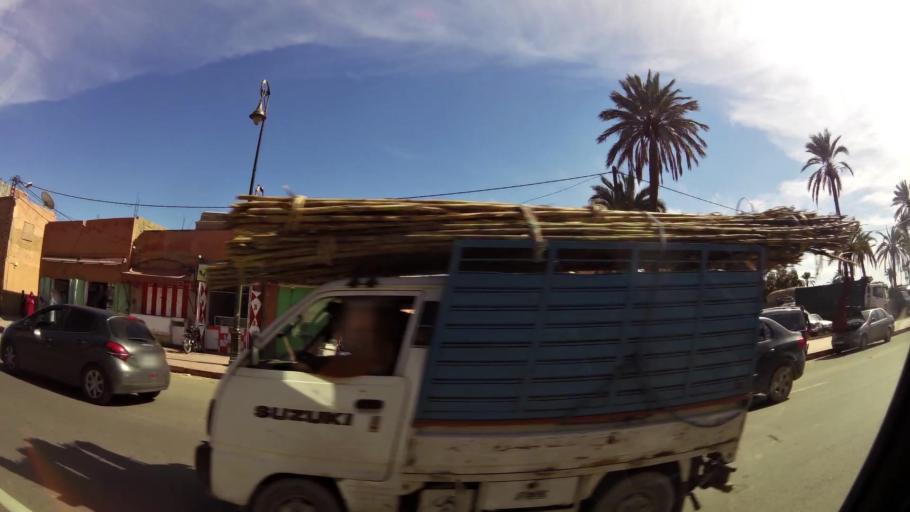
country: MA
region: Marrakech-Tensift-Al Haouz
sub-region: Marrakech
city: Marrakesh
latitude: 31.6450
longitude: -7.9834
